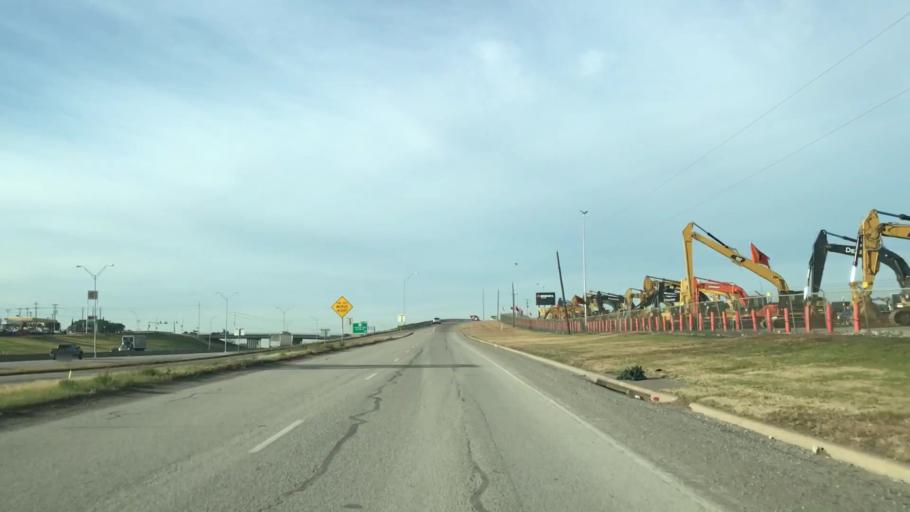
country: US
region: Texas
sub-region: Tarrant County
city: Sansom Park
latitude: 32.8165
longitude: -97.4084
